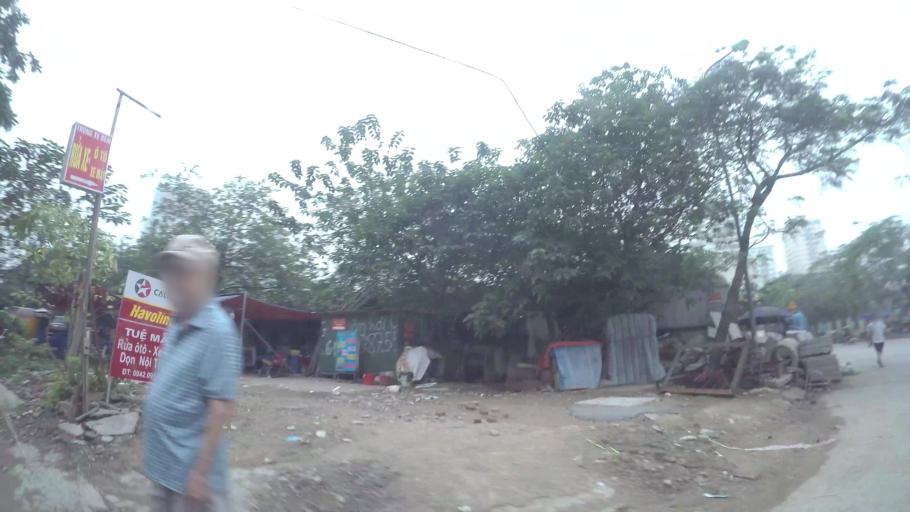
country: VN
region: Ha Noi
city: Hai BaTrung
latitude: 20.9865
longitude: 105.8544
